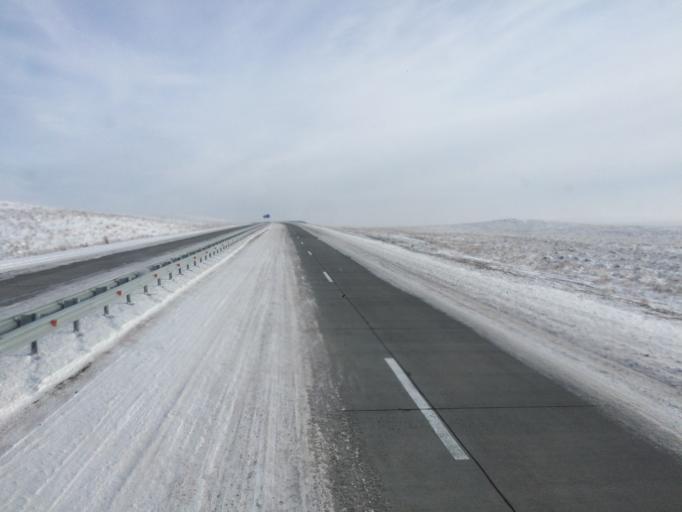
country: KZ
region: Zhambyl
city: Georgiyevka
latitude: 43.3401
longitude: 74.4576
